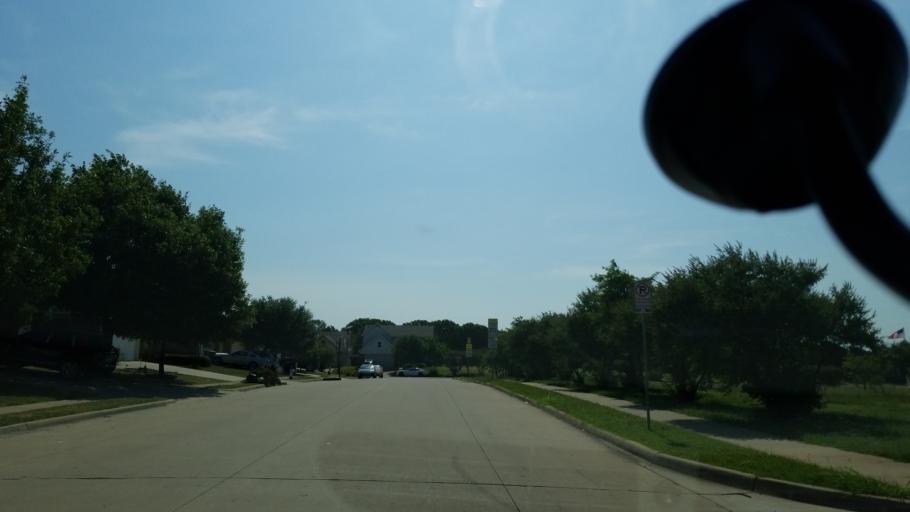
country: US
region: Texas
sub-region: Dallas County
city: Cockrell Hill
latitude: 32.7120
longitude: -96.8673
